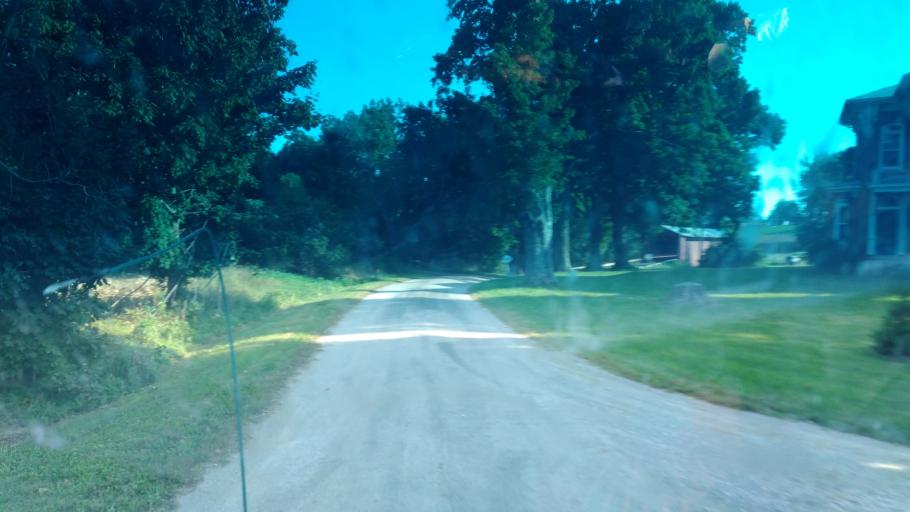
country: US
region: Ohio
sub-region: Wyandot County
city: Upper Sandusky
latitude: 40.9043
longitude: -83.2447
